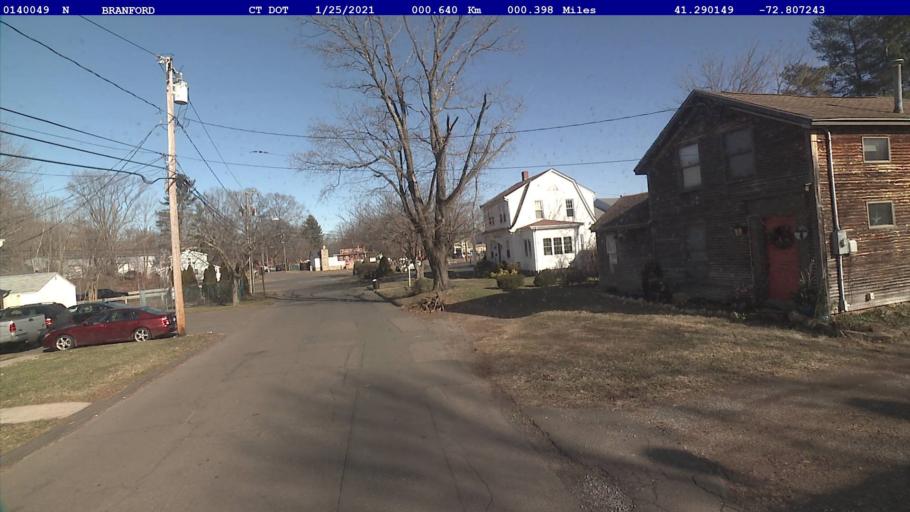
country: US
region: Connecticut
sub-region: New Haven County
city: Branford
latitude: 41.2902
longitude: -72.8072
